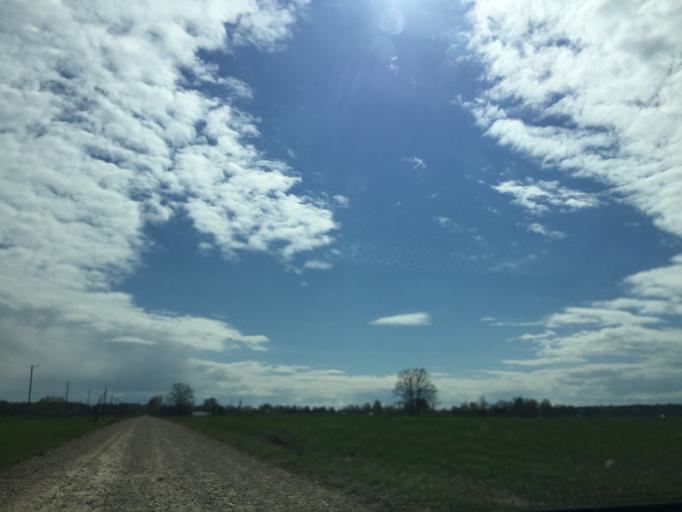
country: LV
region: Jelgava
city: Jelgava
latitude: 56.5706
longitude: 23.7836
